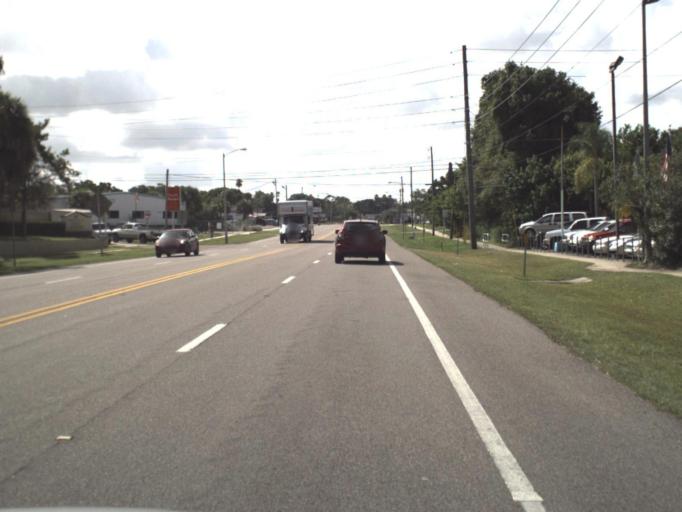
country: US
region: Florida
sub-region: Pinellas County
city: Belleair
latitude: 27.9396
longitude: -82.7981
